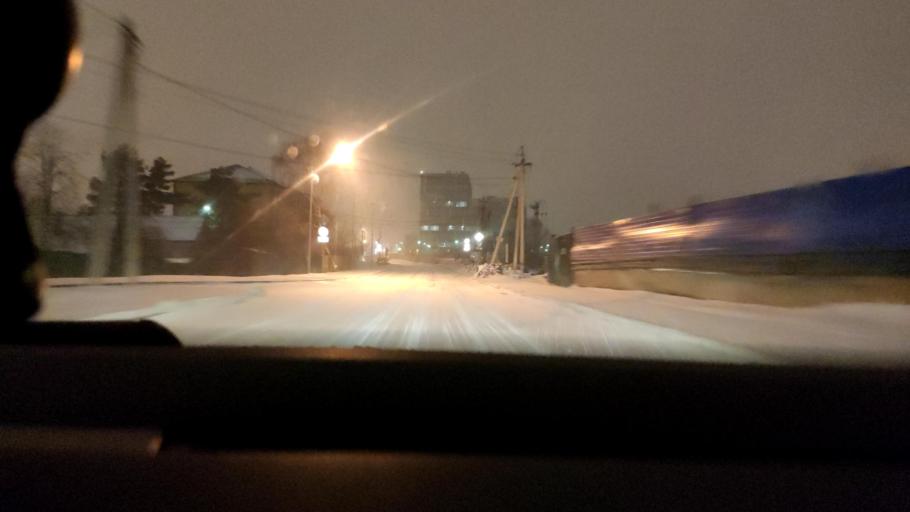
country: RU
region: Moskovskaya
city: Mosrentgen
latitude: 55.6298
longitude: 37.4554
